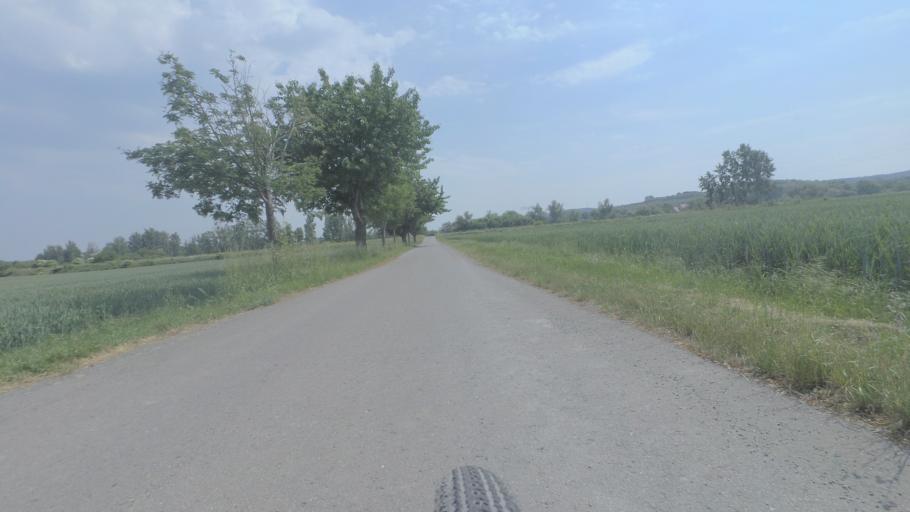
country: DE
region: Saxony-Anhalt
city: Bad Suderode
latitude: 51.7441
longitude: 11.1232
